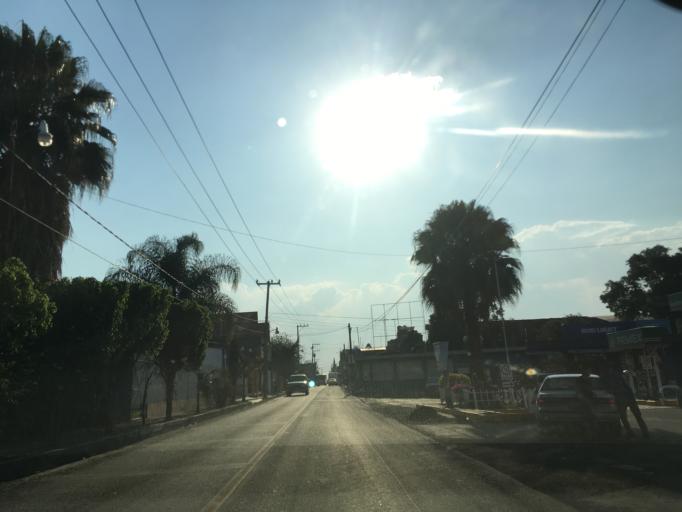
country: MX
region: Michoacan
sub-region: Indaparapeo
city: Colonia de Guadalupe
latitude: 19.8076
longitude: -100.8826
